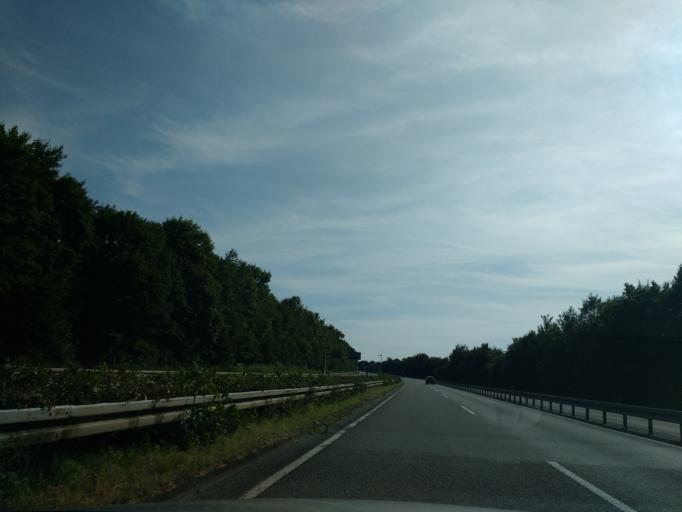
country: DE
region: North Rhine-Westphalia
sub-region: Regierungsbezirk Detmold
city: Wunnenberg
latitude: 51.5804
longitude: 8.7177
